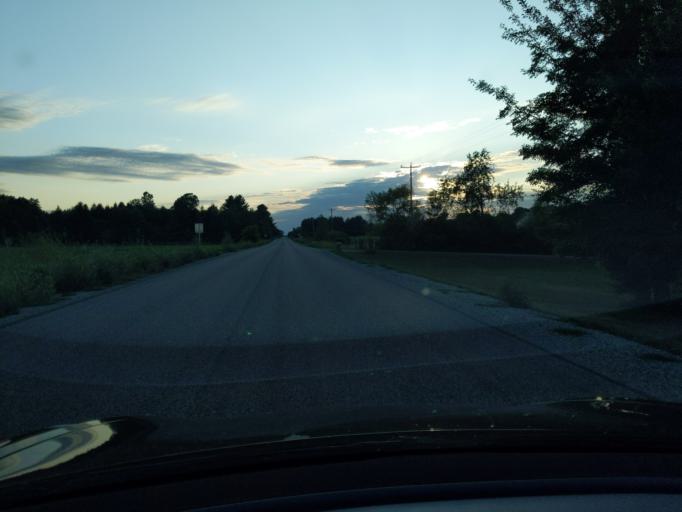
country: US
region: Michigan
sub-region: Gratiot County
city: Saint Louis
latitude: 43.3788
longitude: -84.5819
